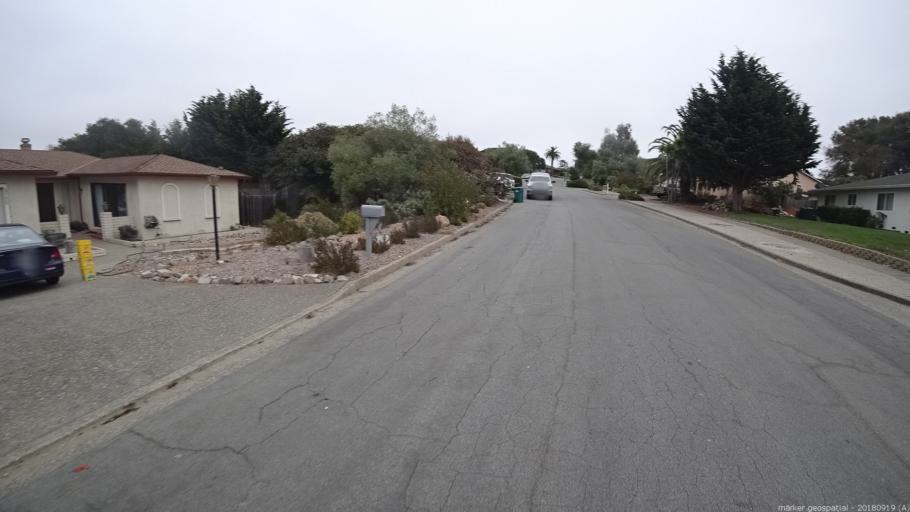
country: US
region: California
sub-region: Monterey County
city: Castroville
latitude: 36.7783
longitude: -121.7223
